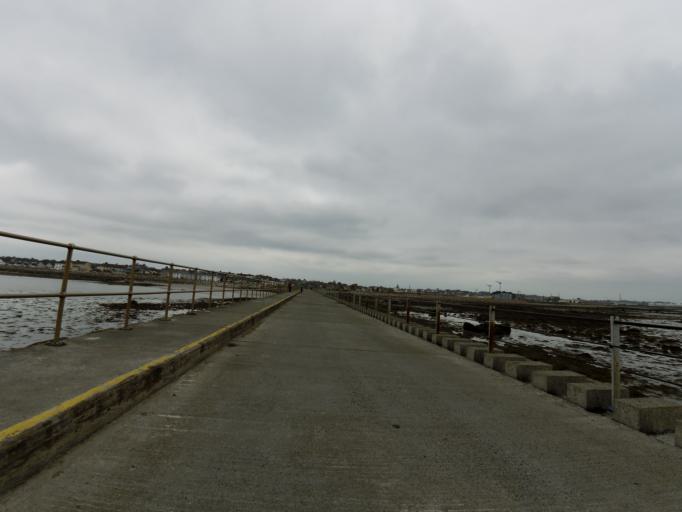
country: IE
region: Connaught
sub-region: County Galway
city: Gaillimh
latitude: 53.2609
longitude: -9.0560
